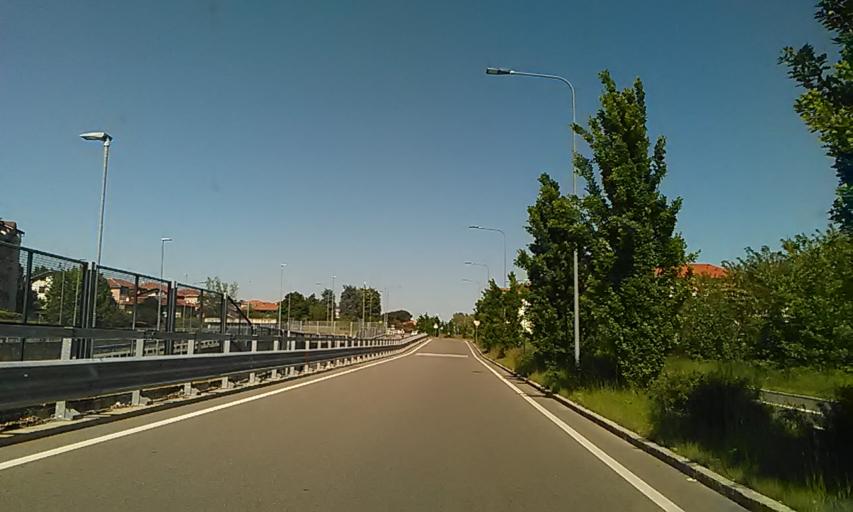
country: IT
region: Piedmont
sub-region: Provincia di Biella
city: Ponderano
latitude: 45.5476
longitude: 8.0627
